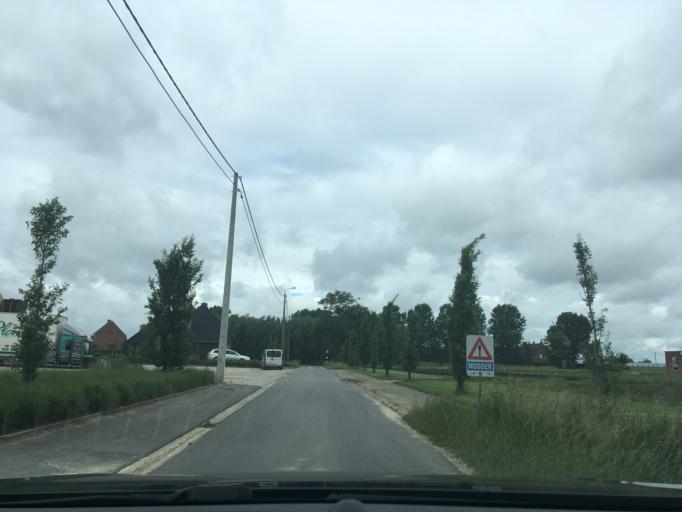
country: BE
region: Flanders
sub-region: Provincie West-Vlaanderen
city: Hooglede
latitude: 50.9517
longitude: 3.0758
